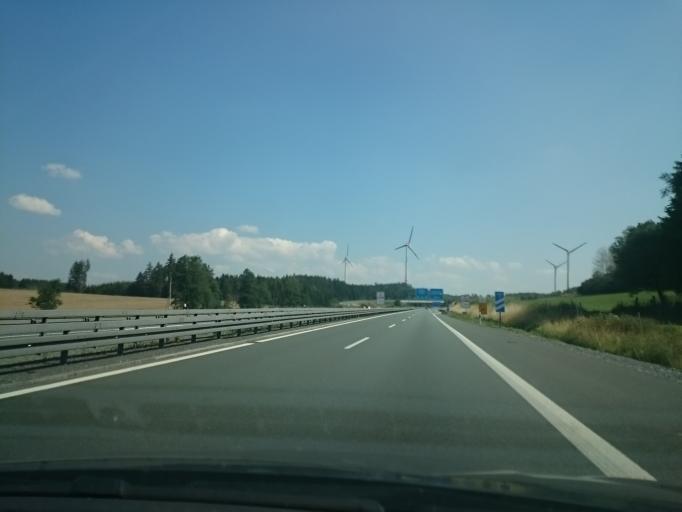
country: DE
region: Bavaria
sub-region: Upper Franconia
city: Trogen
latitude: 50.3793
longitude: 11.9522
